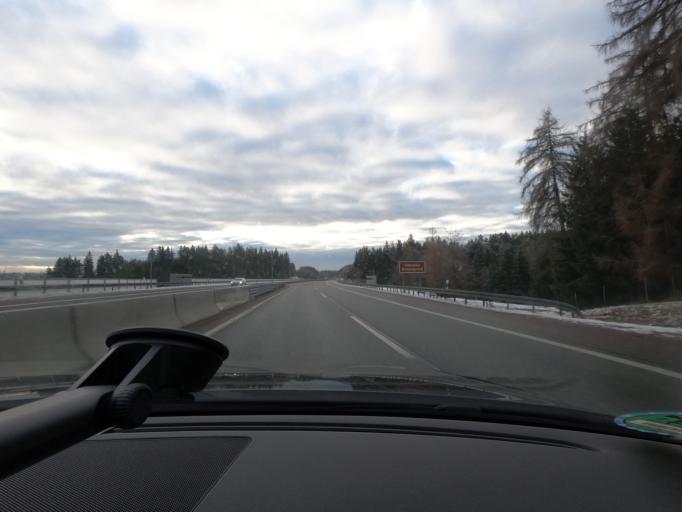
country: DE
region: Thuringia
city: Sankt Kilian
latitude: 50.5438
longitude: 10.7387
